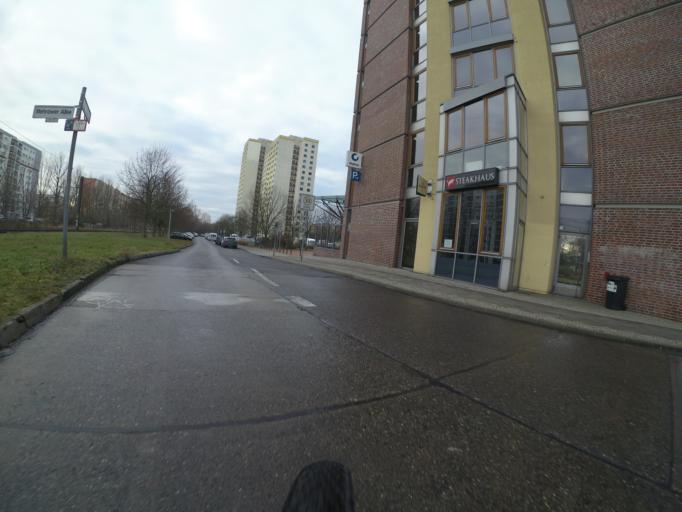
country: DE
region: Berlin
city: Marzahn
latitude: 52.5547
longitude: 13.5669
